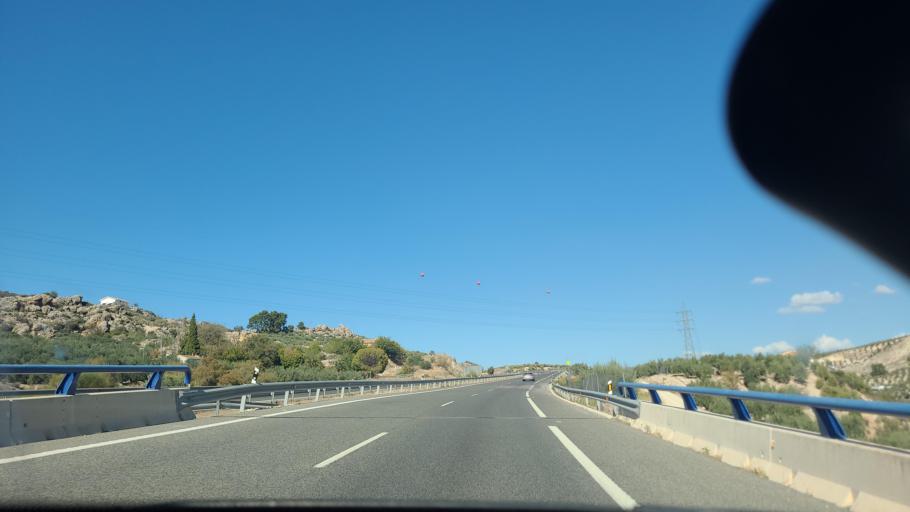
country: ES
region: Andalusia
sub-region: Provincia de Jaen
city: La Guardia de Jaen
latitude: 37.7367
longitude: -3.6852
